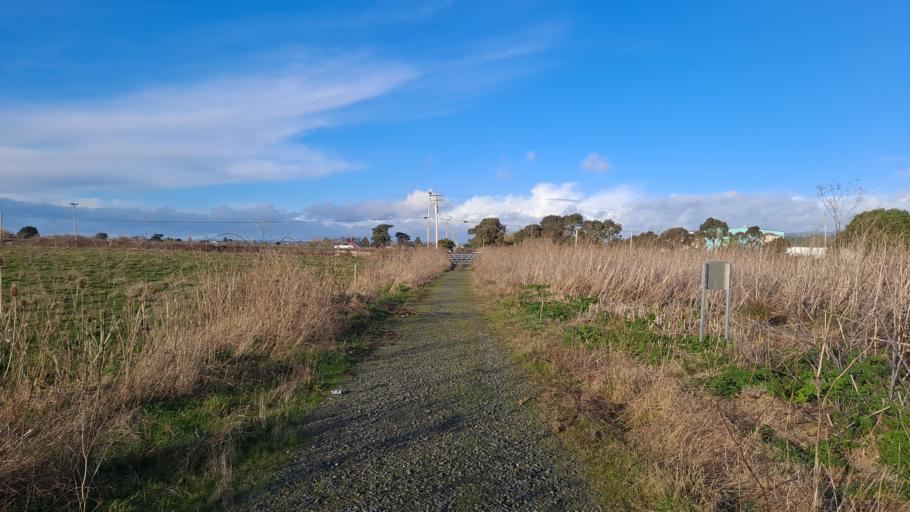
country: US
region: California
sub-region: Humboldt County
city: Arcata
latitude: 40.8657
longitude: -124.0982
